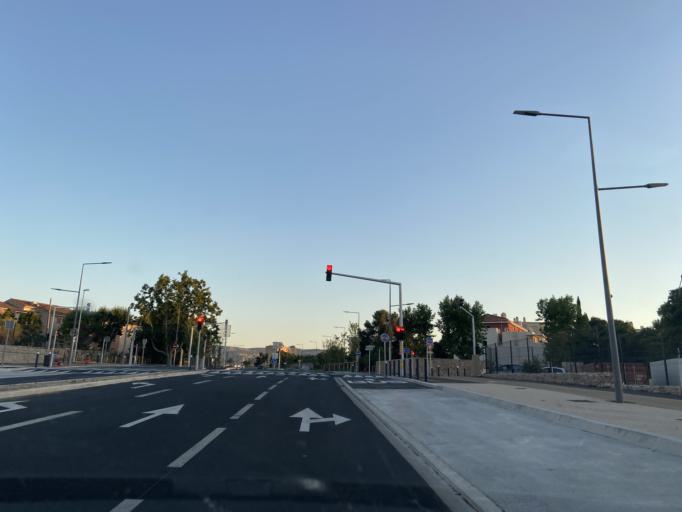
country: FR
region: Provence-Alpes-Cote d'Azur
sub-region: Departement des Bouches-du-Rhone
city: Marseille 10
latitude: 43.2719
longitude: 5.4223
